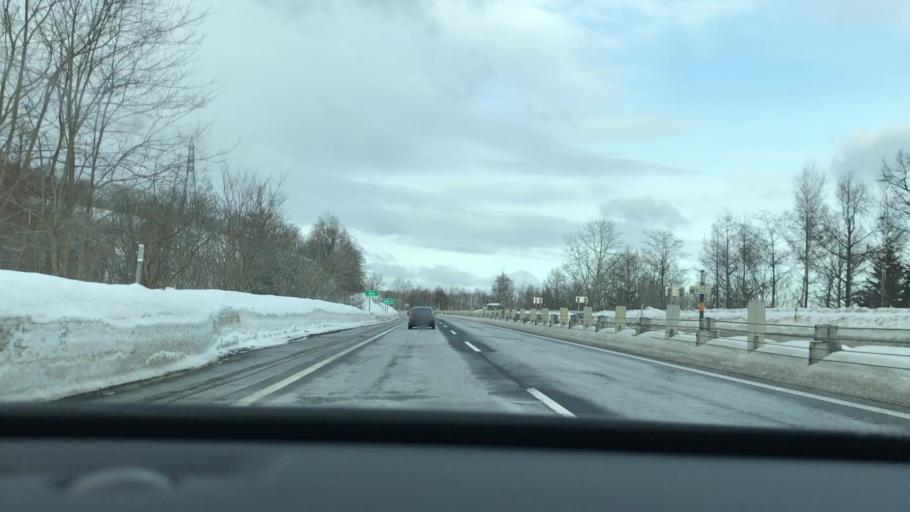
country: JP
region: Hokkaido
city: Otaru
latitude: 43.1388
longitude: 141.1547
